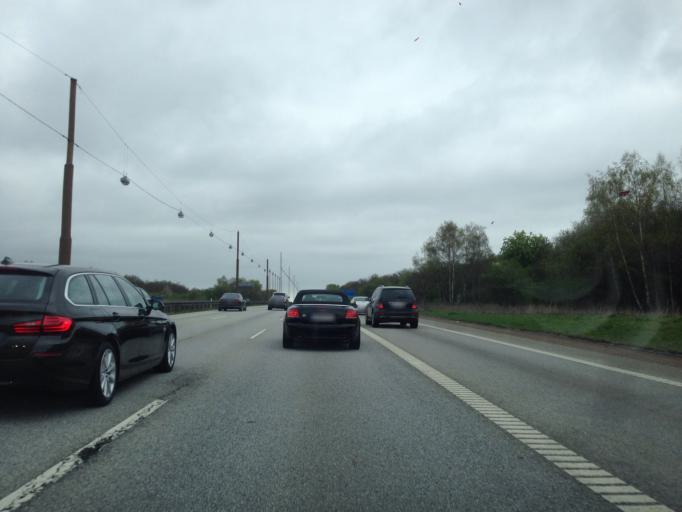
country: DK
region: Capital Region
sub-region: Lyngby-Tarbaek Kommune
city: Kongens Lyngby
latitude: 55.7778
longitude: 12.5255
